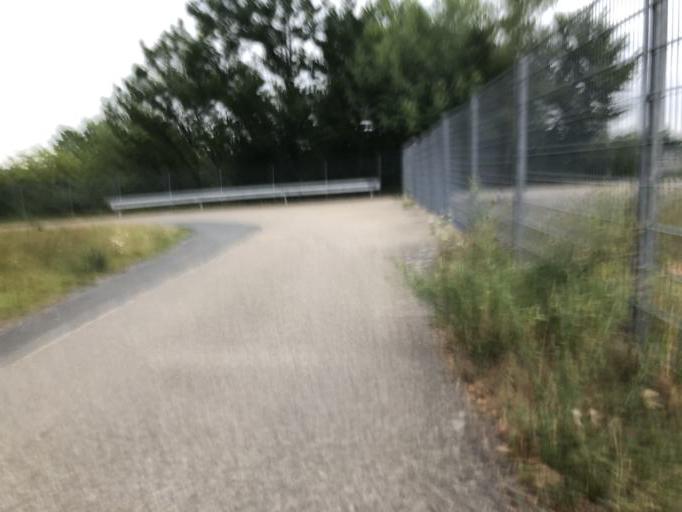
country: DE
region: Bavaria
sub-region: Regierungsbezirk Mittelfranken
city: Erlangen
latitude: 49.5540
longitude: 10.9693
